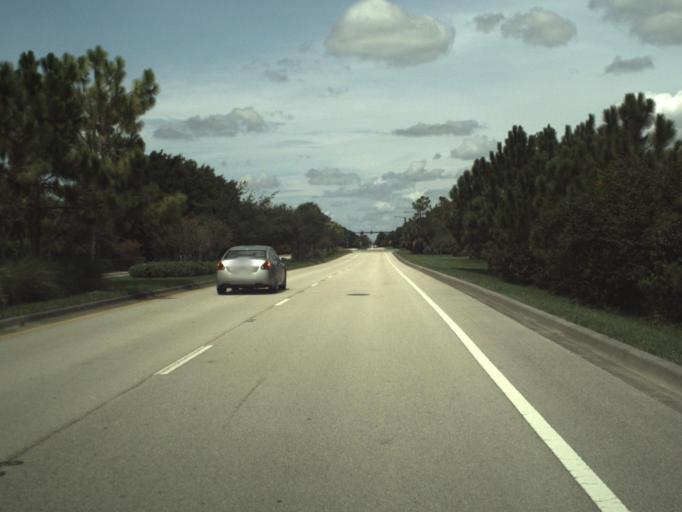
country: US
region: Florida
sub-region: Palm Beach County
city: Palm Beach Gardens
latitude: 26.8396
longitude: -80.1474
